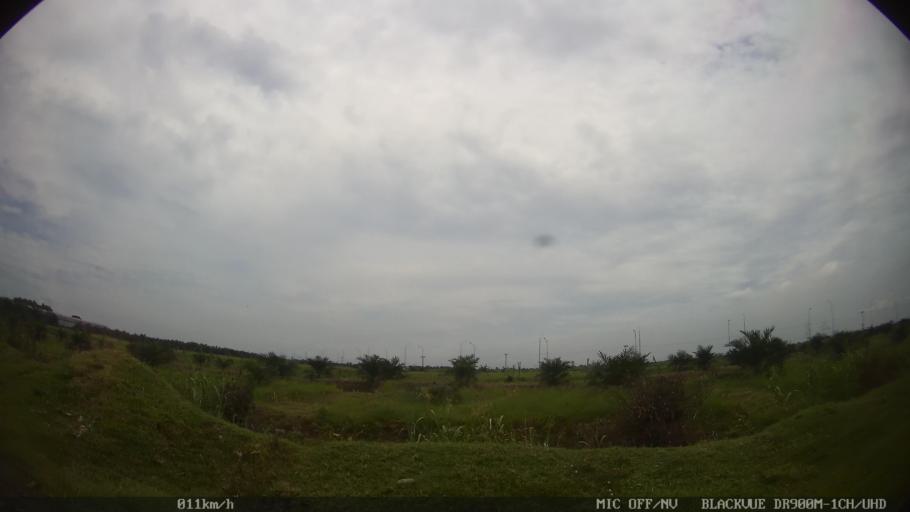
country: ID
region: North Sumatra
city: Sunggal
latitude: 3.6279
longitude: 98.5808
